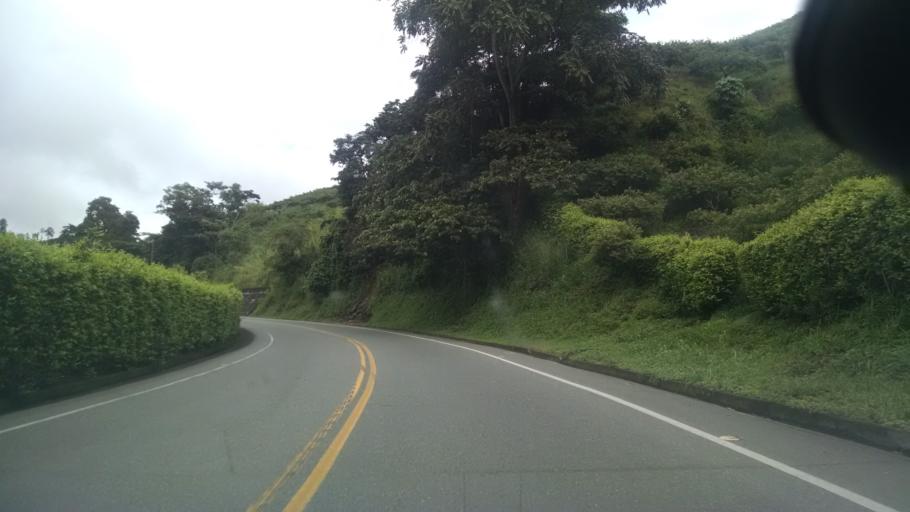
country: CO
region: Caldas
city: Palestina
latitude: 5.0638
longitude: -75.6149
